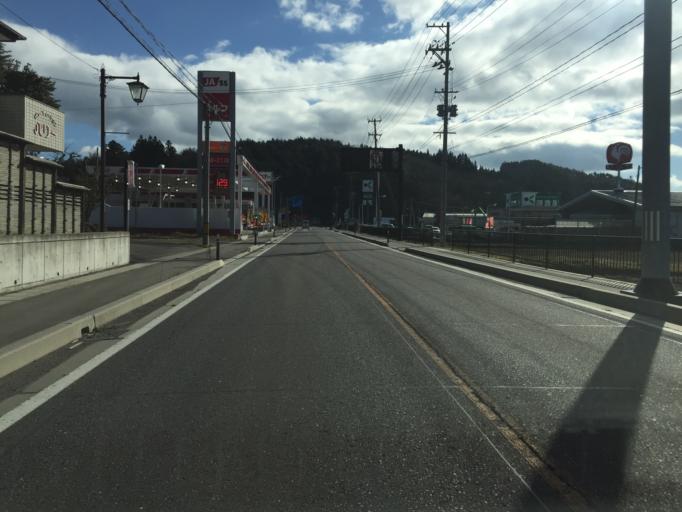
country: JP
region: Fukushima
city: Ishikawa
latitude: 37.2376
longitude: 140.5705
